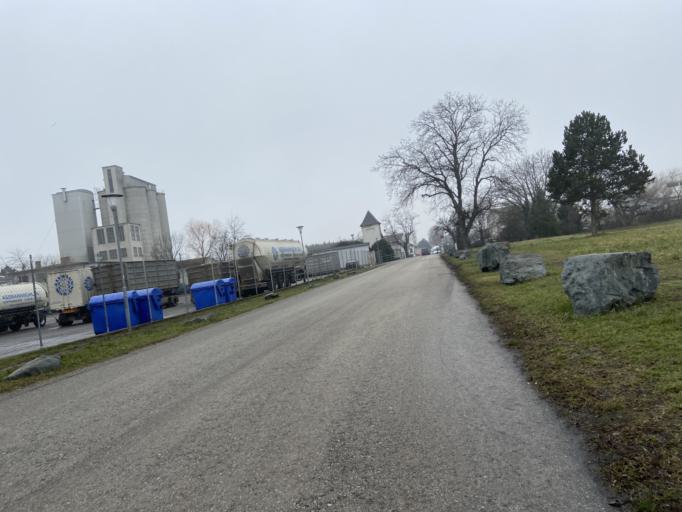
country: AT
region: Lower Austria
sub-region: Politischer Bezirk Modling
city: Guntramsdorf
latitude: 48.0438
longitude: 16.3152
